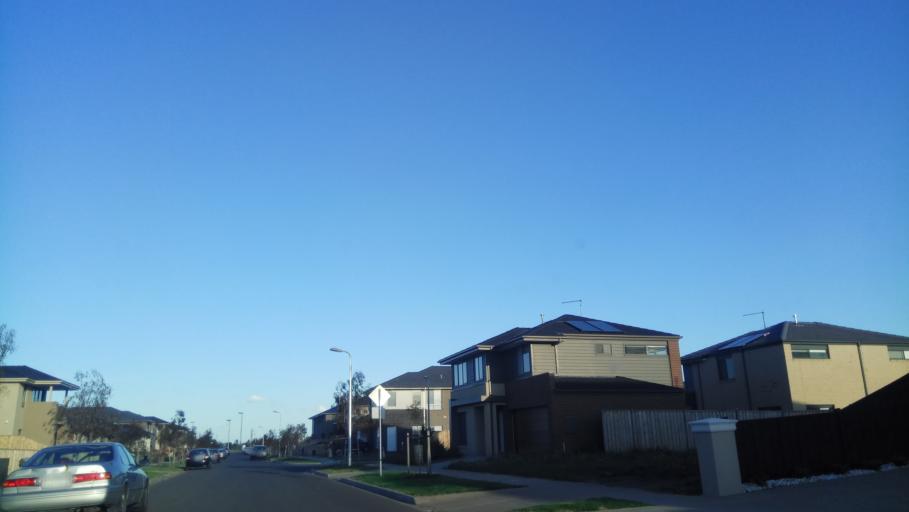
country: AU
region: Victoria
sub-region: Wyndham
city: Point Cook
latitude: -37.9086
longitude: 144.7474
